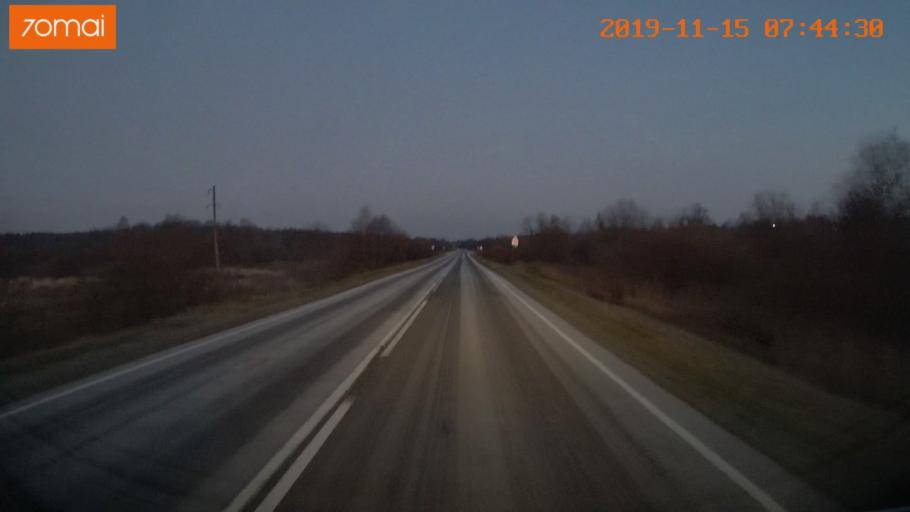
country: RU
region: Vologda
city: Sheksna
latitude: 58.8140
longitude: 38.3122
